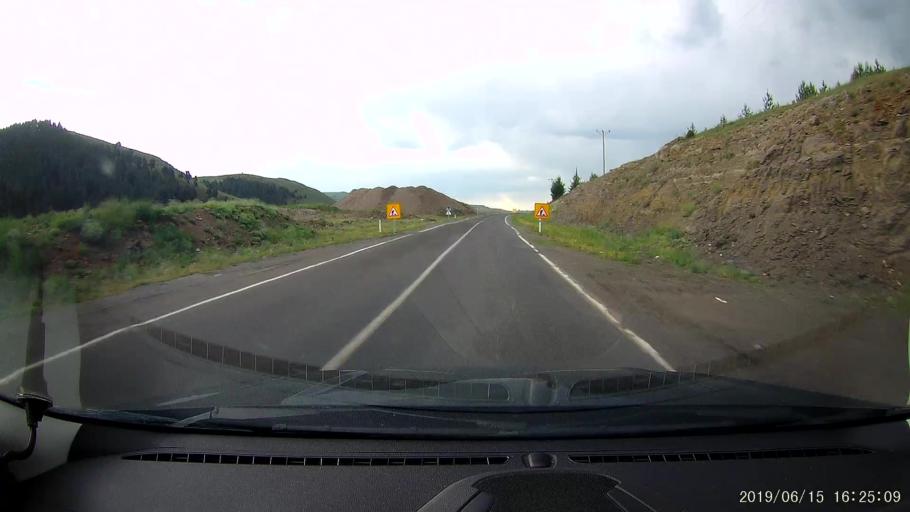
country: TR
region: Ardahan
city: Hanak
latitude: 41.1574
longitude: 42.8714
